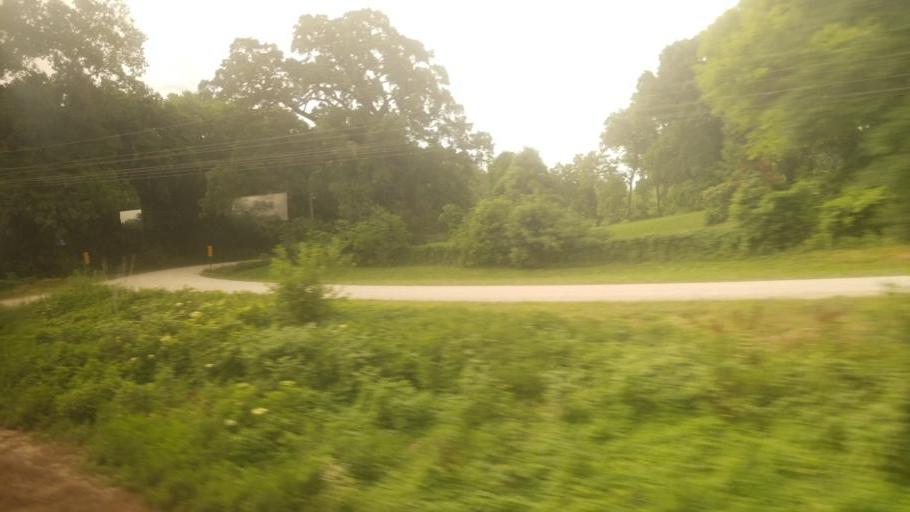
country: US
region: Kansas
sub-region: Jefferson County
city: Oskaloosa
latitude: 39.0577
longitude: -95.4105
